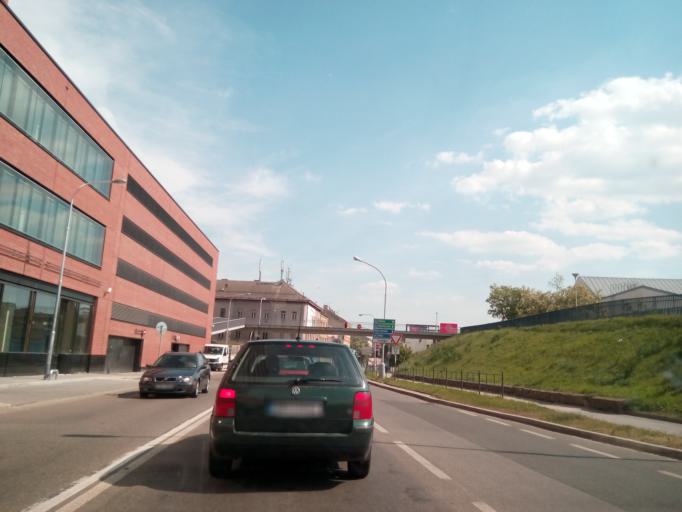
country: CZ
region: South Moravian
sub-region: Mesto Brno
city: Brno
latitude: 49.1876
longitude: 16.6168
